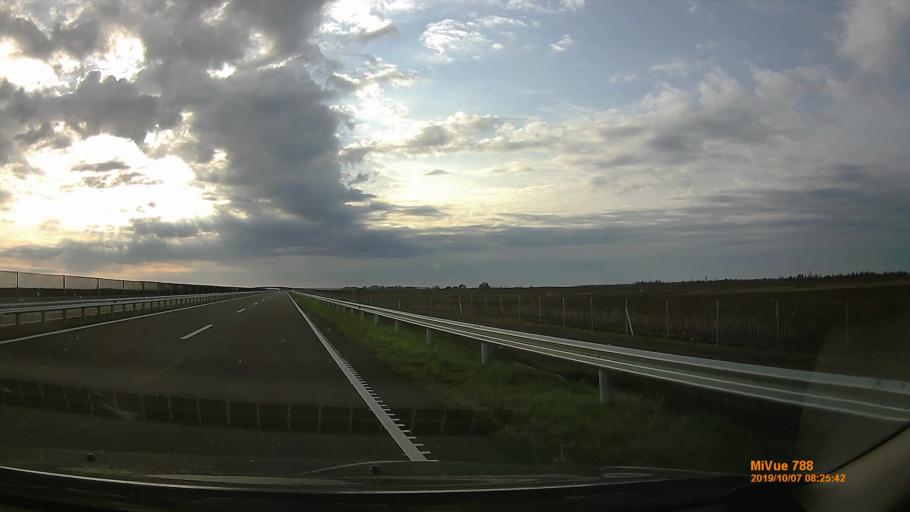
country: HU
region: Jasz-Nagykun-Szolnok
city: Kunszentmarton
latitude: 46.8269
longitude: 20.3602
